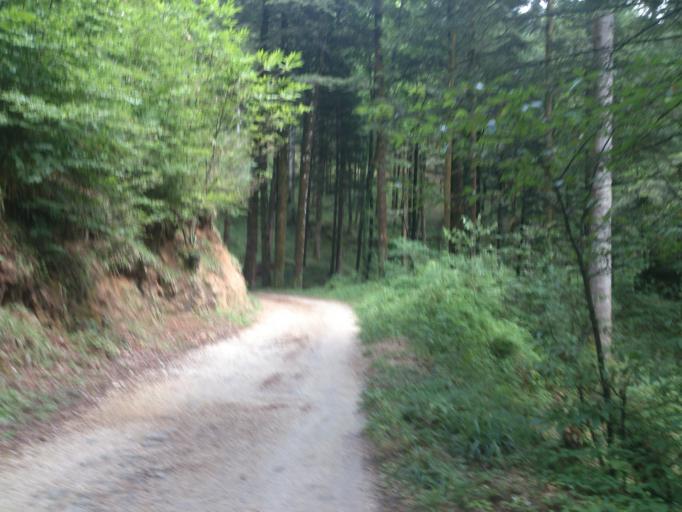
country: IT
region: Calabria
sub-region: Provincia di Vibo-Valentia
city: Serra San Bruno
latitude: 38.5513
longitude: 16.3103
